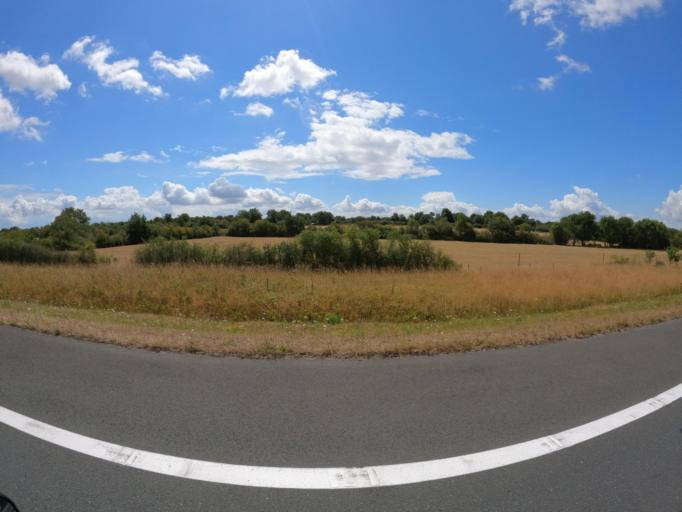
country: FR
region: Pays de la Loire
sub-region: Departement de Maine-et-Loire
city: Saint-Georges-sur-Loire
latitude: 47.4403
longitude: -0.7552
